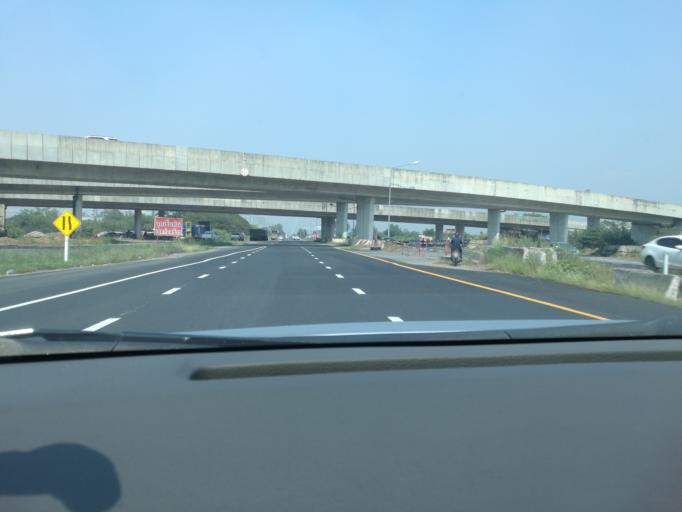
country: TH
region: Sara Buri
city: Saraburi
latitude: 14.5618
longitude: 100.9049
